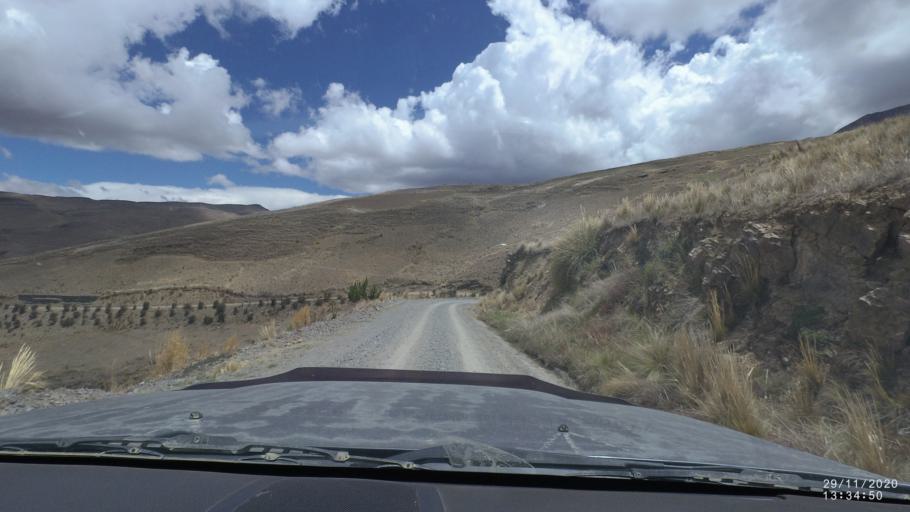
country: BO
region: Cochabamba
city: Cochabamba
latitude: -17.1120
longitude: -66.3345
